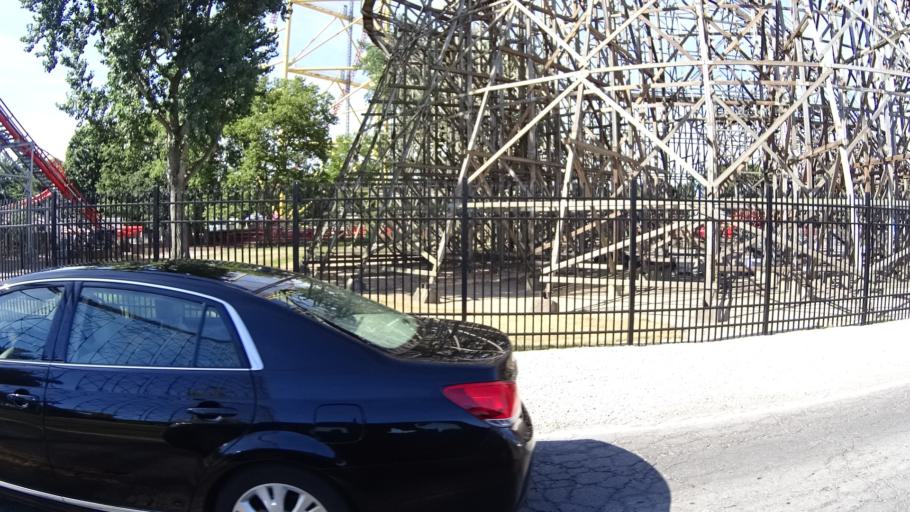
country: US
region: Ohio
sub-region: Erie County
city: Sandusky
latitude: 41.4862
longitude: -82.6867
